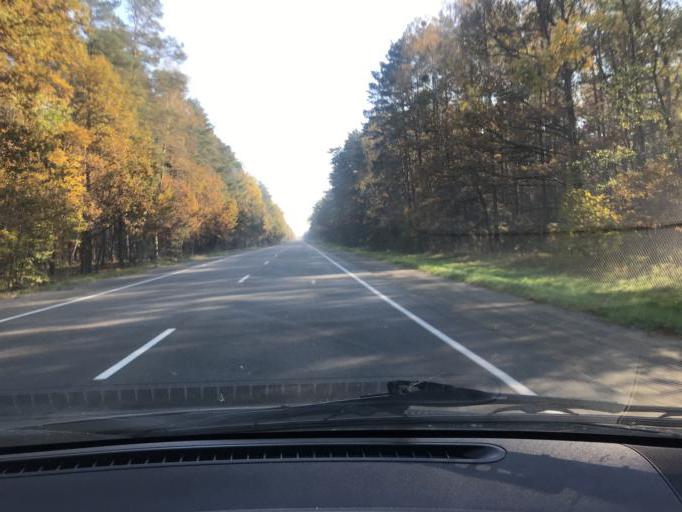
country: BY
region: Brest
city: Horad Luninyets
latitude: 52.2859
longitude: 26.7993
